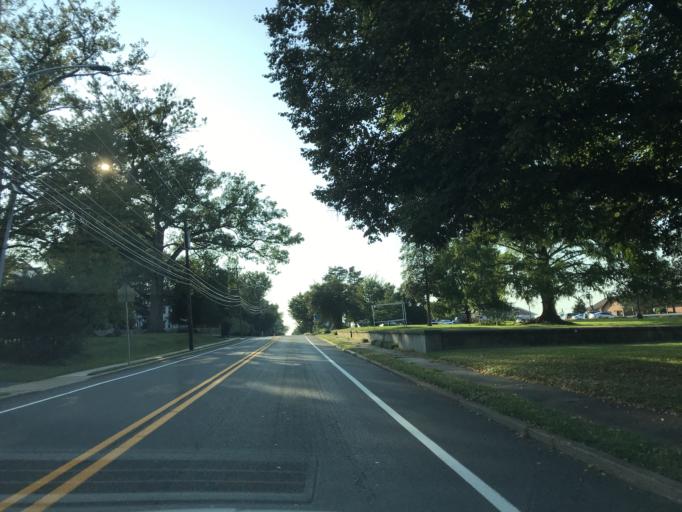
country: US
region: Delaware
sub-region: New Castle County
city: Newark
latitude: 39.6856
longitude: -75.7631
